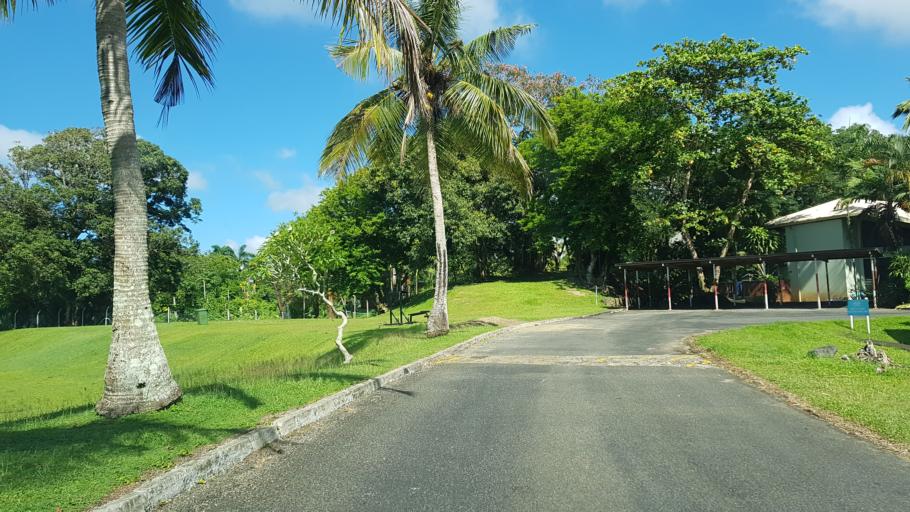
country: FJ
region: Central
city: Suva
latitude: -18.1514
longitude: 178.4409
